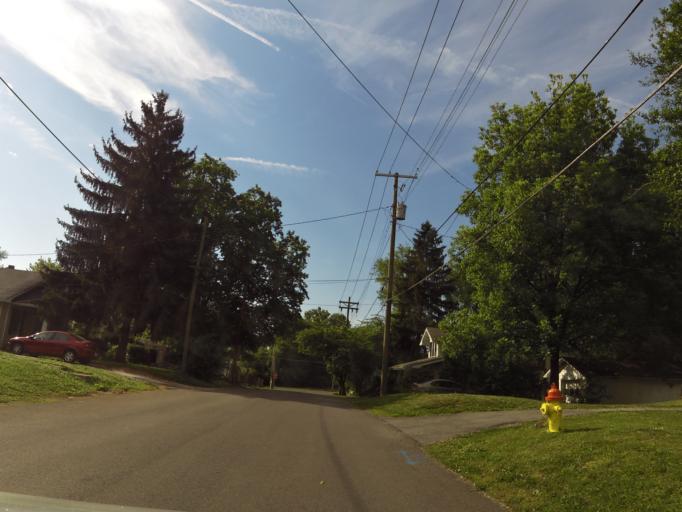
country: US
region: Tennessee
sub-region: Knox County
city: Knoxville
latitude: 35.9989
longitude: -83.9182
